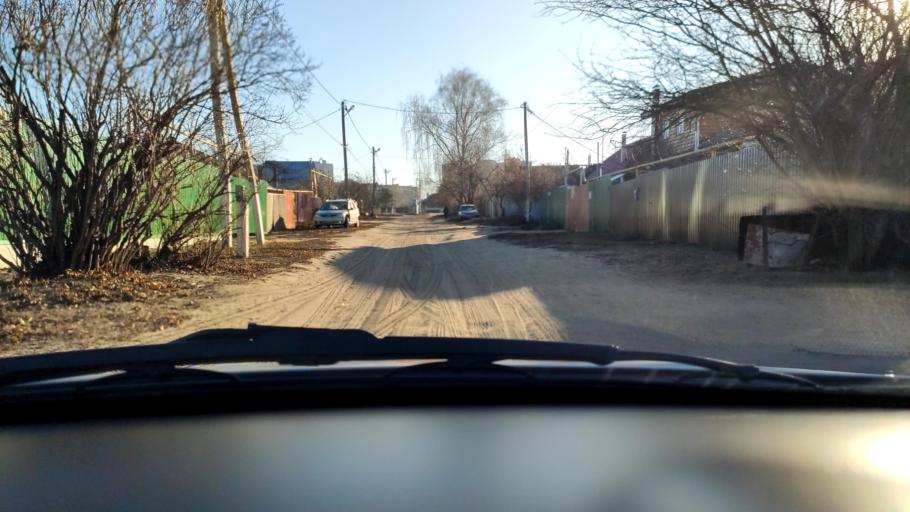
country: RU
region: Voronezj
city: Podgornoye
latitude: 51.7296
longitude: 39.1564
